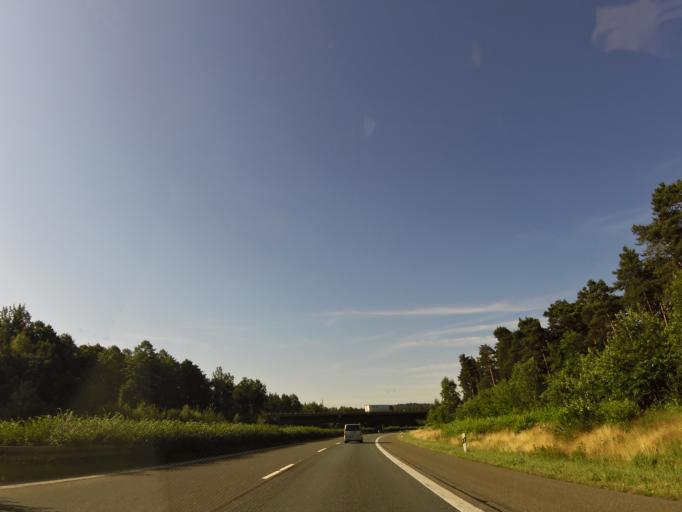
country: DE
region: Bavaria
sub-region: Regierungsbezirk Mittelfranken
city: Rothenbach an der Pegnitz
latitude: 49.4562
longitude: 11.2382
